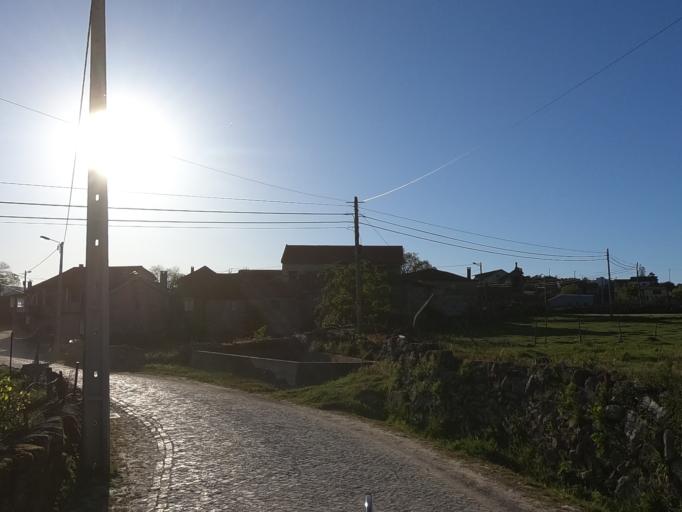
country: PT
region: Vila Real
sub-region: Vila Real
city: Vila Real
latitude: 41.3610
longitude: -7.6512
